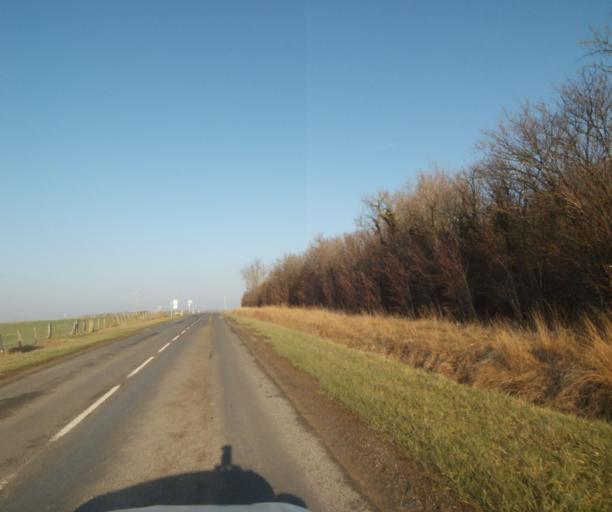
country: FR
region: Champagne-Ardenne
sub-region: Departement de la Haute-Marne
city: Montier-en-Der
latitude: 48.4947
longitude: 4.7547
